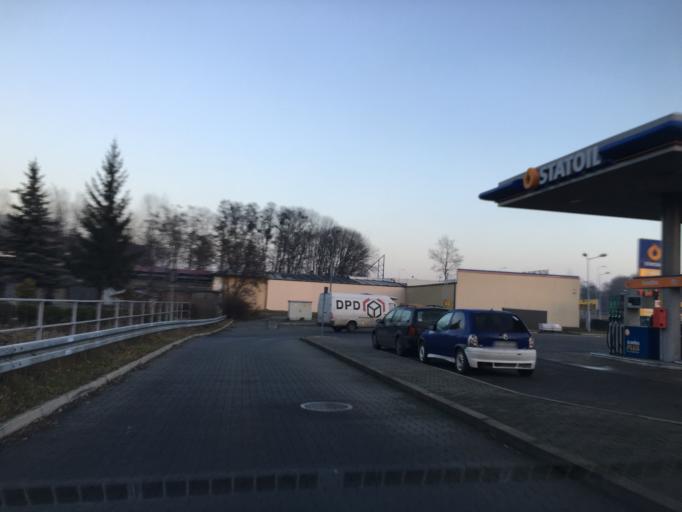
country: PL
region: Silesian Voivodeship
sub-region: Powiat tarnogorski
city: Radzionkow
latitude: 50.3537
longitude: 18.8629
